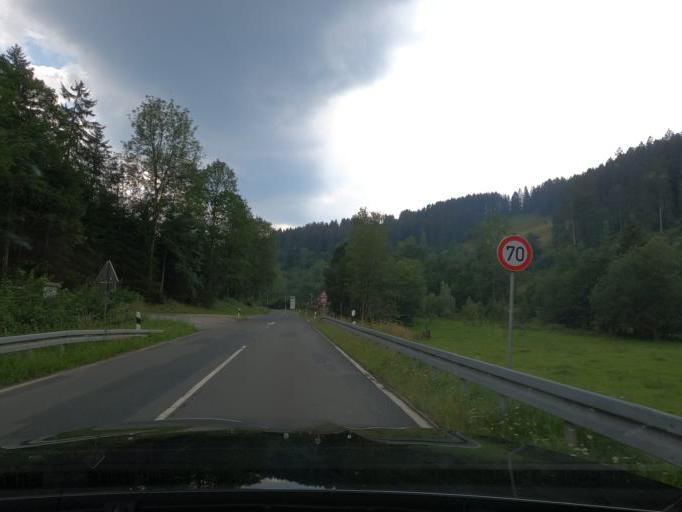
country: DE
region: Lower Saxony
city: Wildemann
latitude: 51.8306
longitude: 10.2715
